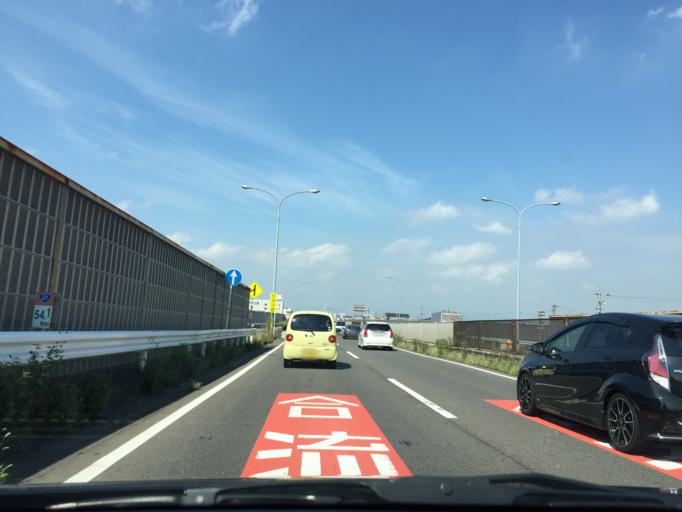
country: JP
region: Gifu
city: Kasamatsucho
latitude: 35.3880
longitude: 136.7623
